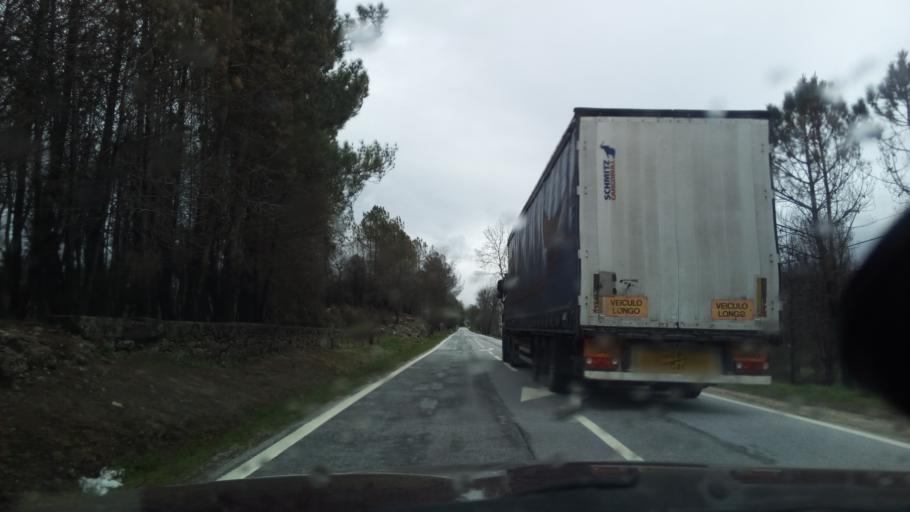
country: PT
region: Guarda
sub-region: Fornos de Algodres
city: Fornos de Algodres
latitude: 40.5561
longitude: -7.4961
